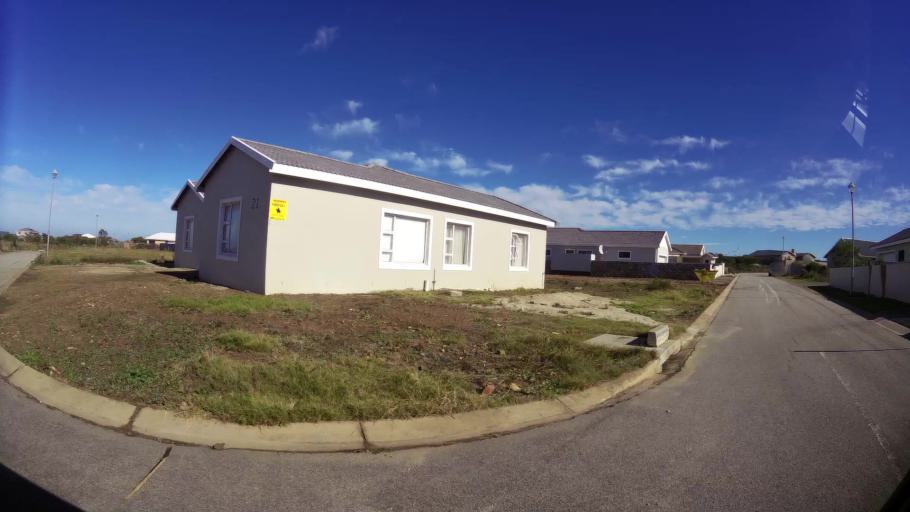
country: ZA
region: Eastern Cape
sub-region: Cacadu District Municipality
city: Jeffrey's Bay
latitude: -34.0319
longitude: 24.9057
